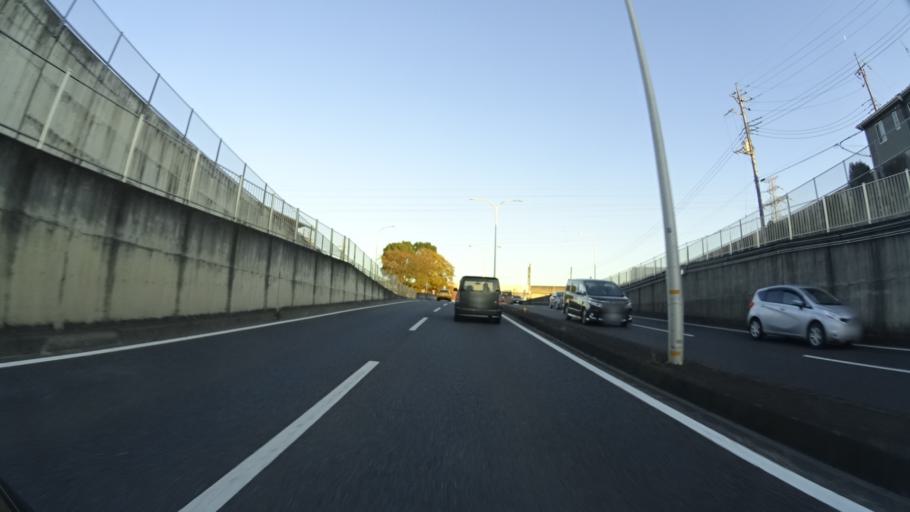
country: JP
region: Tochigi
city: Utsunomiya-shi
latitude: 36.5045
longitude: 139.8797
